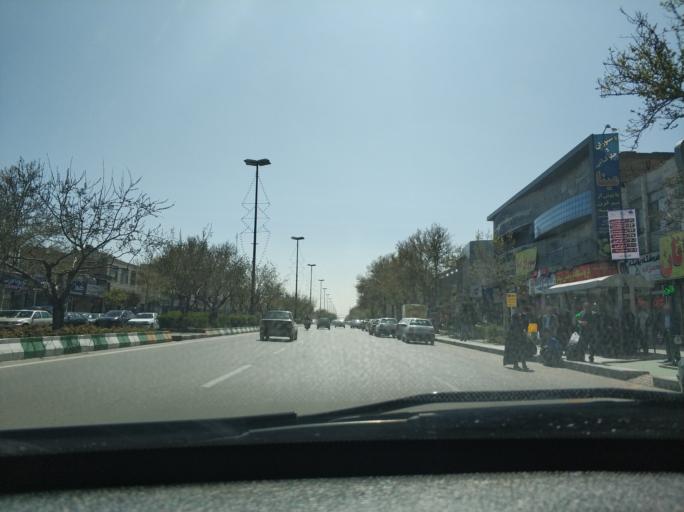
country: IR
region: Razavi Khorasan
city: Mashhad
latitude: 36.2672
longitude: 59.5994
